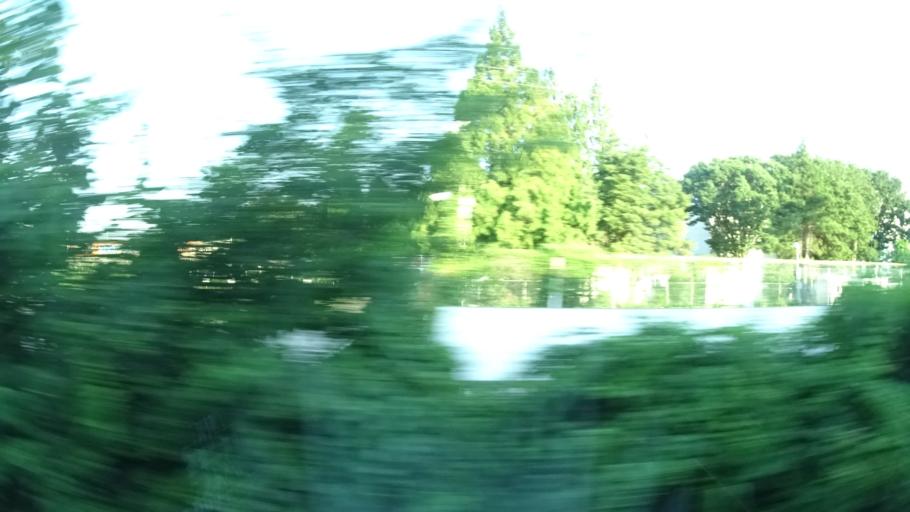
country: JP
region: Ibaraki
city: Ishioka
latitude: 36.1158
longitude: 140.2431
